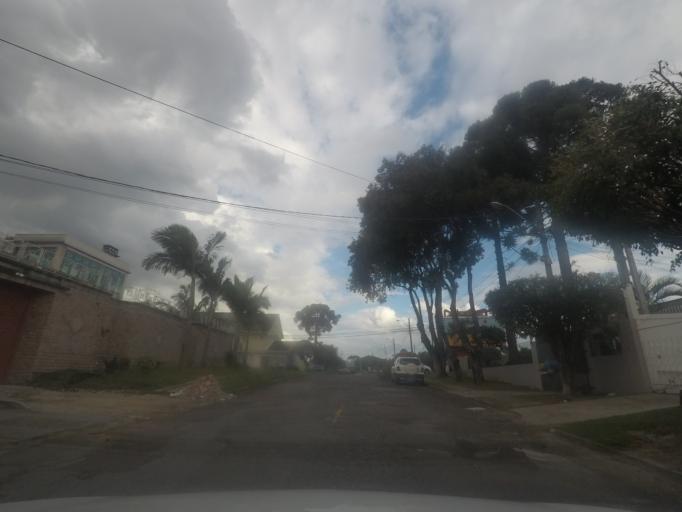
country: BR
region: Parana
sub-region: Pinhais
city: Pinhais
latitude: -25.4679
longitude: -49.2204
